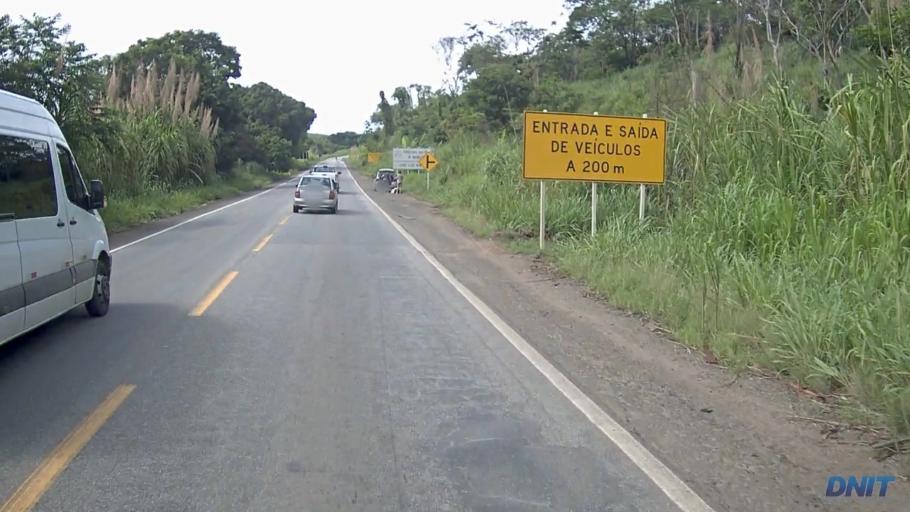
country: BR
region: Minas Gerais
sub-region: Ipaba
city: Ipaba
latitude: -19.3490
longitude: -42.4333
